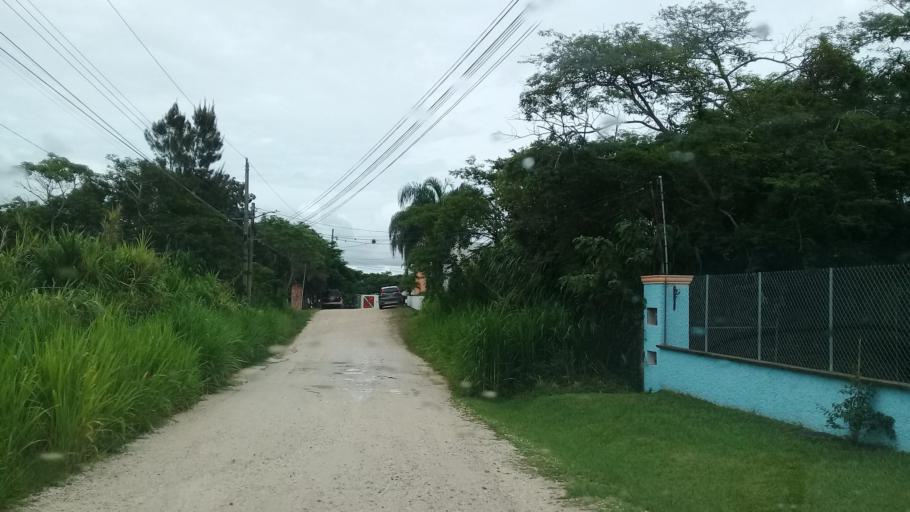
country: MX
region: Veracruz
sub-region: Emiliano Zapata
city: Jacarandas
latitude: 19.5062
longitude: -96.8389
